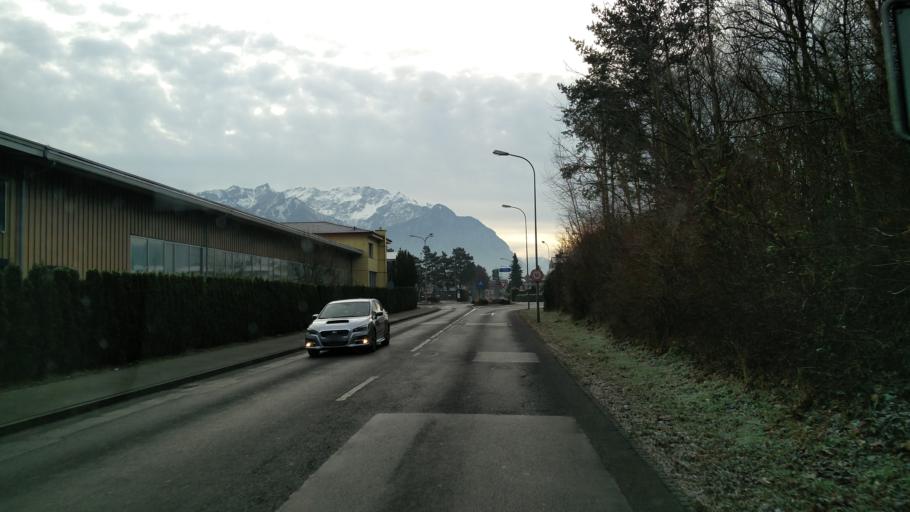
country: CH
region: Saint Gallen
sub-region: Wahlkreis Werdenberg
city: Buchs
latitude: 47.1612
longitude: 9.4790
